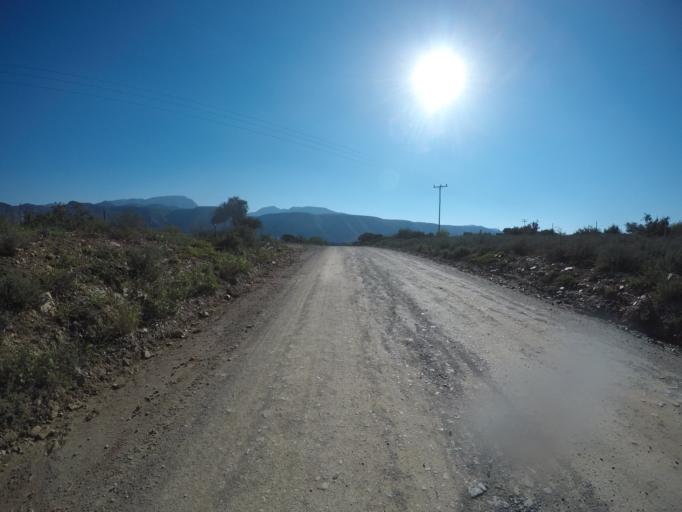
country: ZA
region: Eastern Cape
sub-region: Cacadu District Municipality
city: Kruisfontein
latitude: -33.6723
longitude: 24.5766
